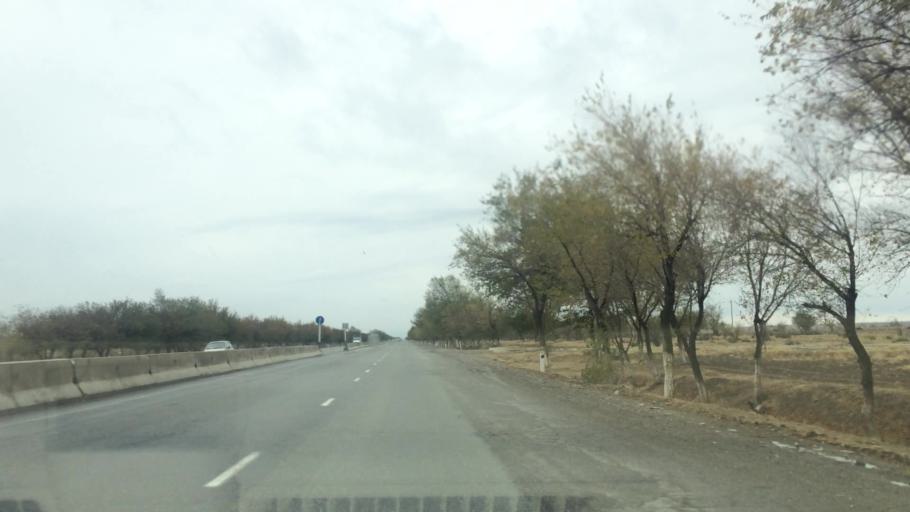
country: UZ
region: Samarqand
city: Bulung'ur
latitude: 39.8361
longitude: 67.4250
